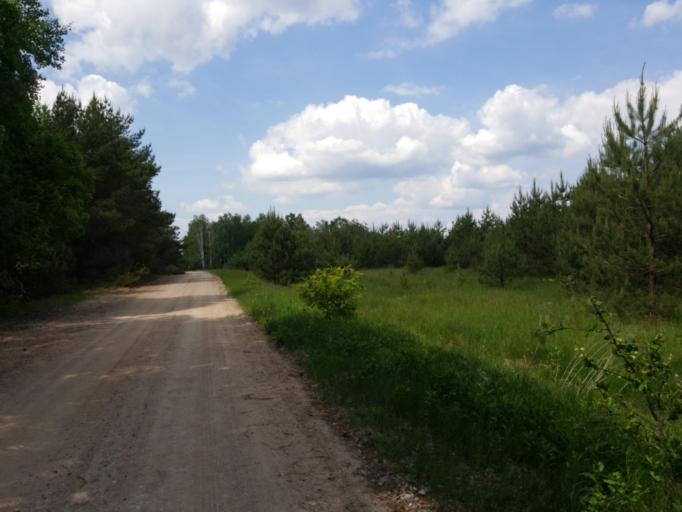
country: BY
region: Brest
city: Kamyanyuki
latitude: 52.5580
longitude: 23.6442
